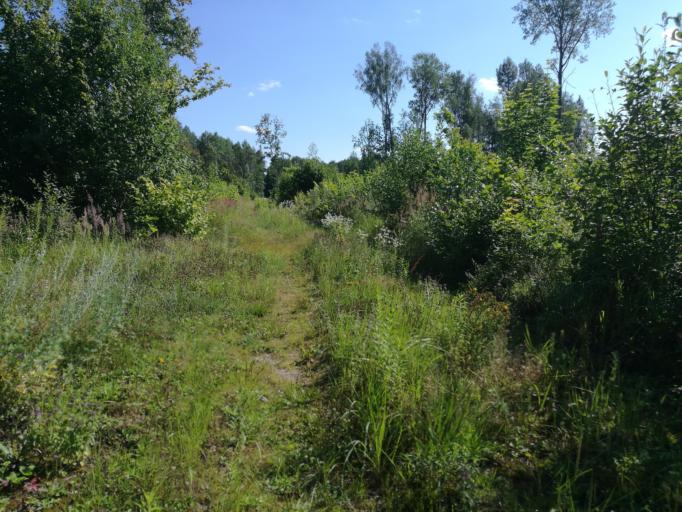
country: BY
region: Minsk
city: Krupki
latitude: 54.0747
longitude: 29.1947
